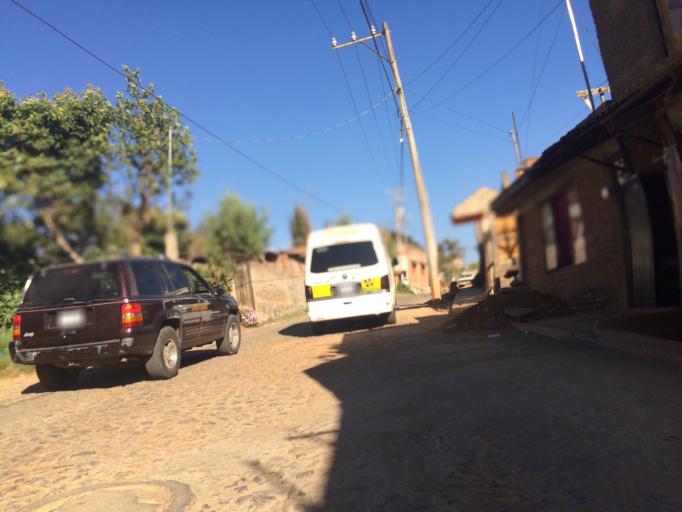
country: MX
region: Michoacan
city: Patzcuaro
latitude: 19.5085
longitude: -101.5989
